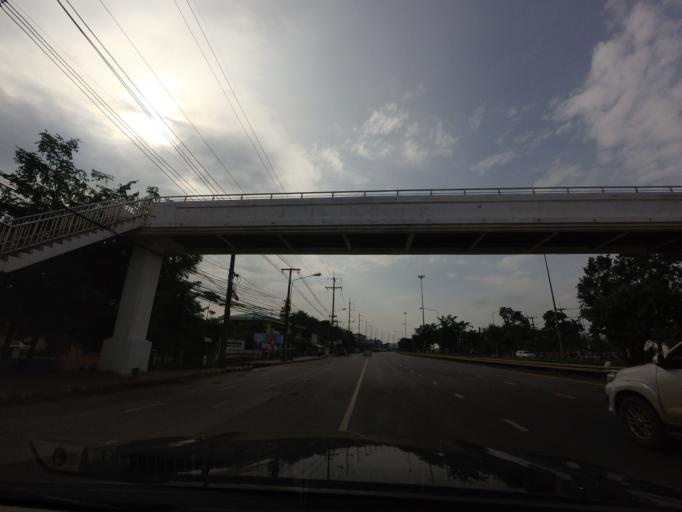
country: TH
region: Nong Khai
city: Nong Khai
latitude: 17.8651
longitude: 102.7480
